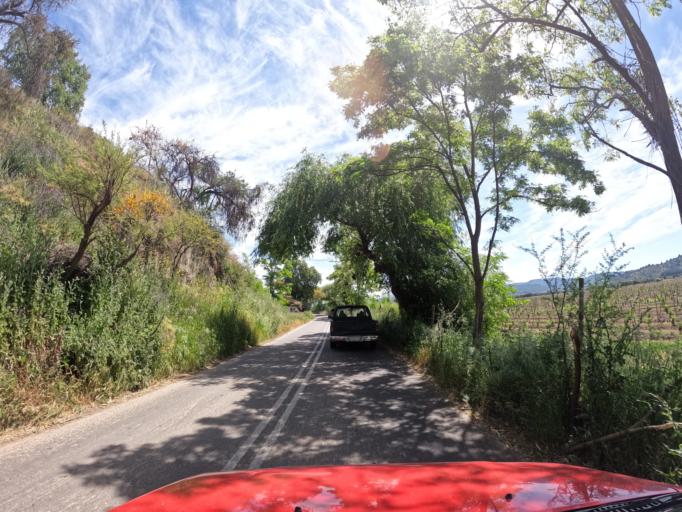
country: CL
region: Maule
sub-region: Provincia de Talca
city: Talca
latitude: -34.9893
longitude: -71.8347
